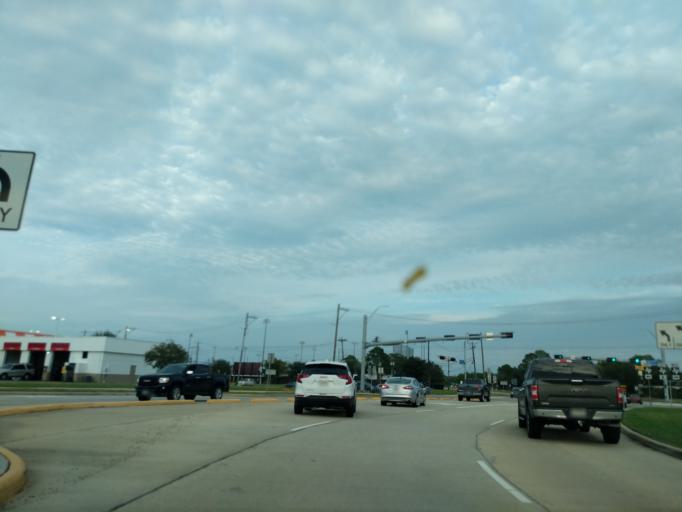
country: US
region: Texas
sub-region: Galveston County
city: League City
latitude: 29.5230
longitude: -95.0773
